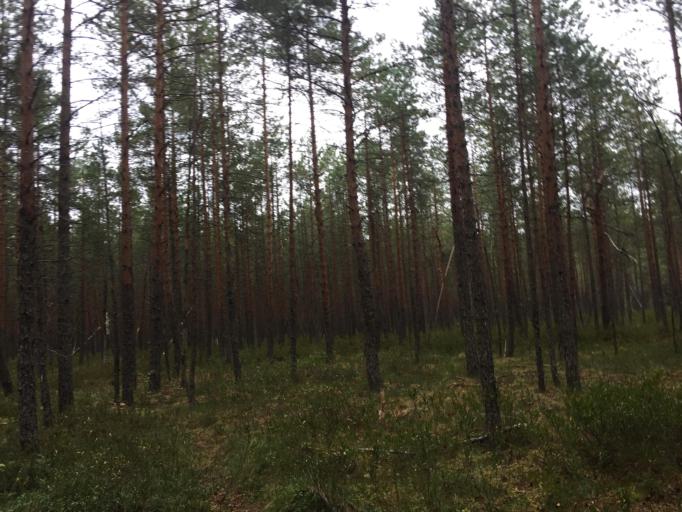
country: RU
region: Leningrad
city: Rozhdestveno
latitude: 59.2915
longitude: 30.0081
